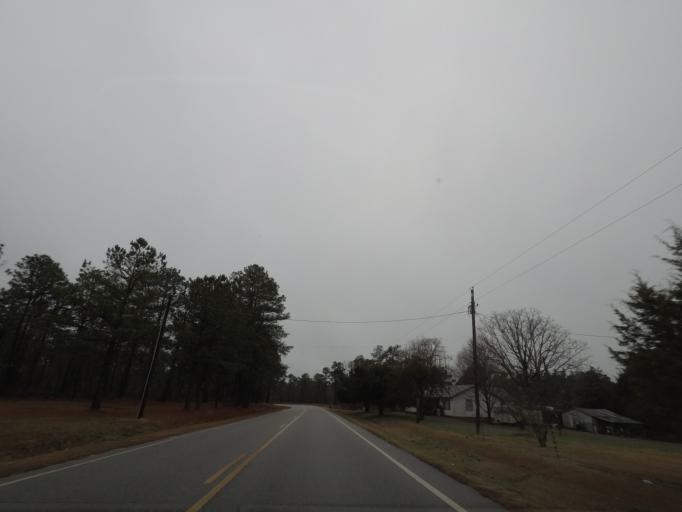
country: US
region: North Carolina
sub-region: Cumberland County
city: Spring Lake
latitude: 35.2744
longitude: -78.9912
